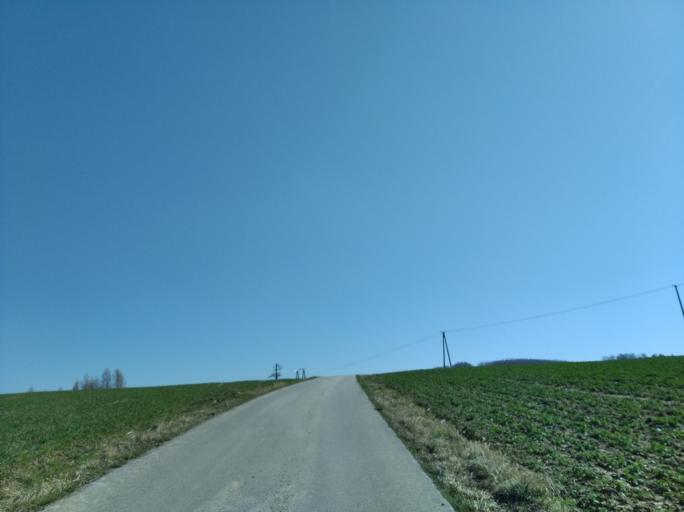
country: PL
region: Subcarpathian Voivodeship
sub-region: Powiat strzyzowski
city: Strzyzow
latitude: 49.8567
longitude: 21.8139
